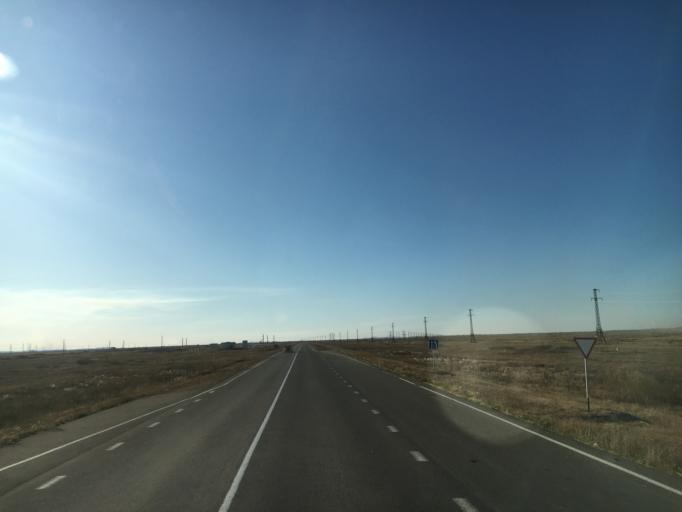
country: KZ
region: Qaraghandy
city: Tokarevka
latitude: 50.0995
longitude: 73.3086
